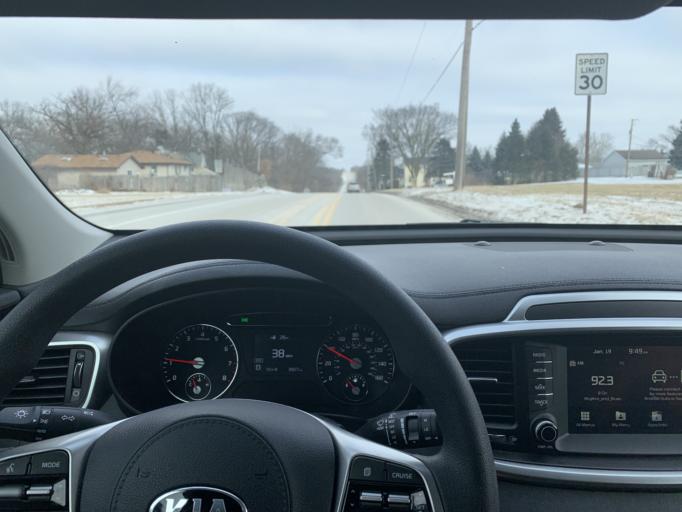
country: US
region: Illinois
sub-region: Will County
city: Ingalls Park
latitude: 41.5415
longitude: -88.0436
